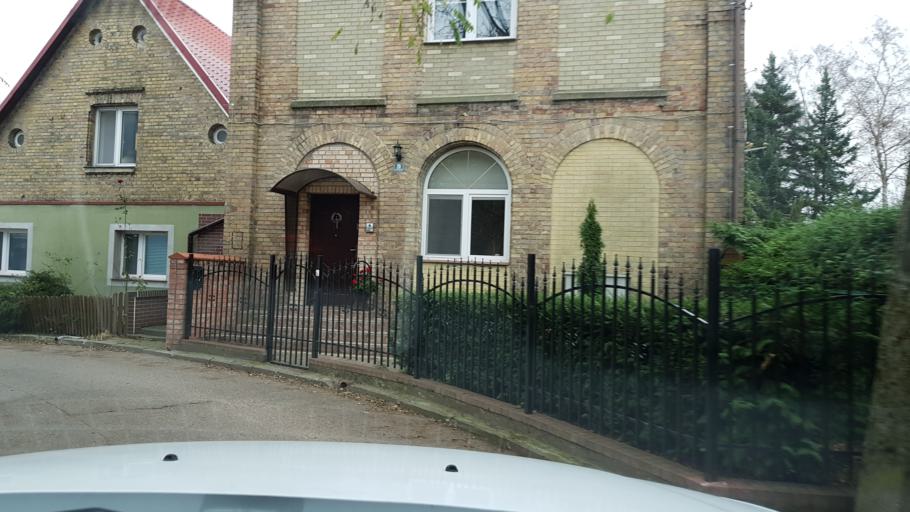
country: PL
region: West Pomeranian Voivodeship
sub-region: Powiat slawienski
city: Darlowo
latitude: 54.4242
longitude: 16.4198
